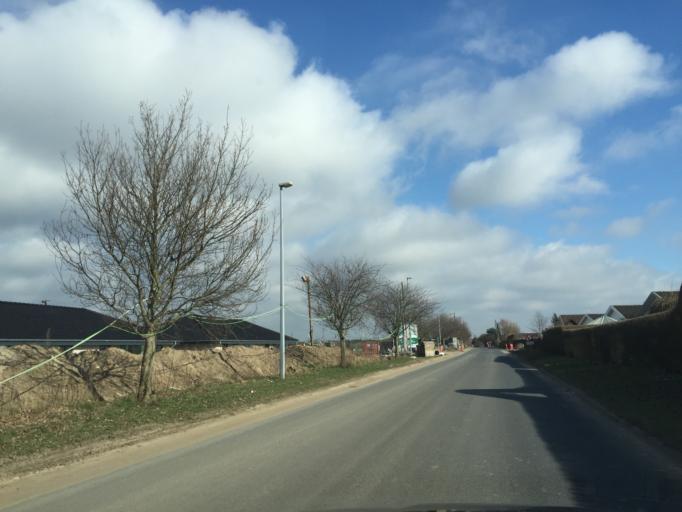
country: DK
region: South Denmark
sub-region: Odense Kommune
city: Neder Holluf
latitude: 55.3875
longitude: 10.4542
